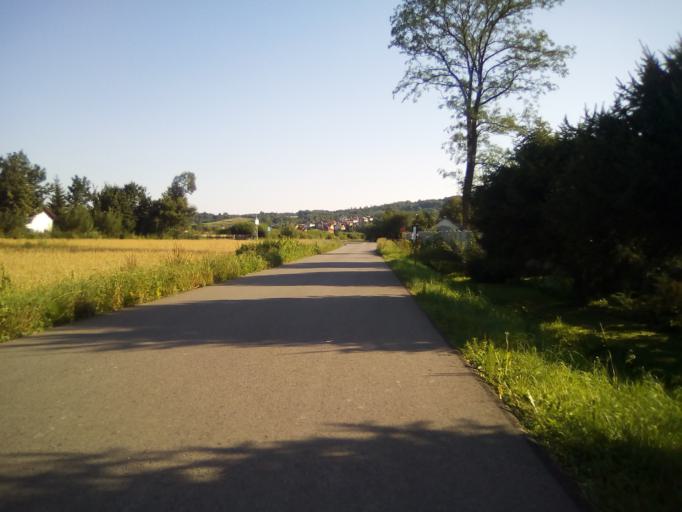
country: PL
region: Subcarpathian Voivodeship
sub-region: Powiat brzozowski
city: Domaradz
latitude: 49.7980
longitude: 21.9382
